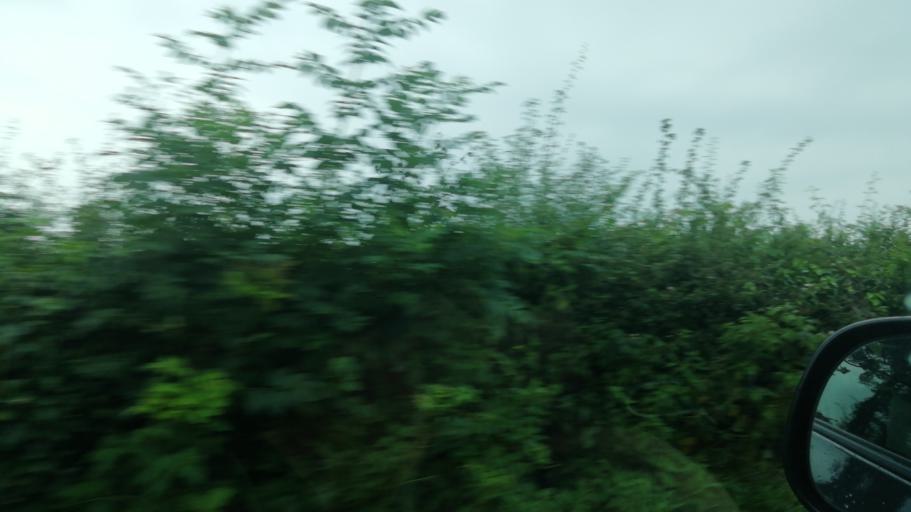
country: IE
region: Leinster
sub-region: Kilkenny
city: Thomastown
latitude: 52.6204
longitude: -7.0895
